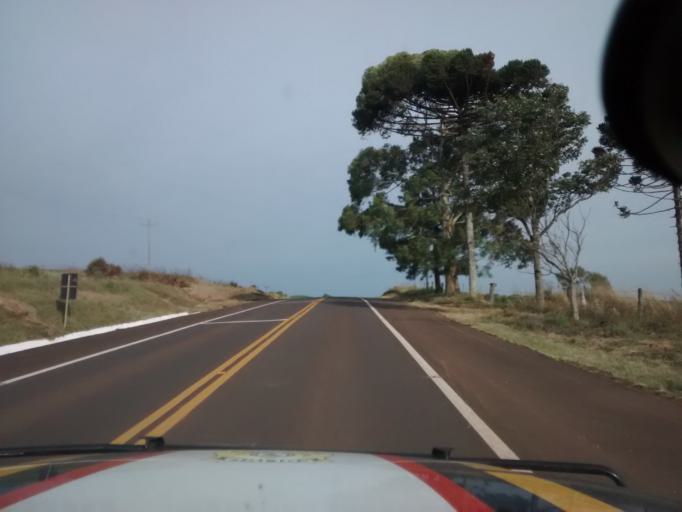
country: BR
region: Rio Grande do Sul
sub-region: Lagoa Vermelha
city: Lagoa Vermelha
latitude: -28.3245
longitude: -51.2545
